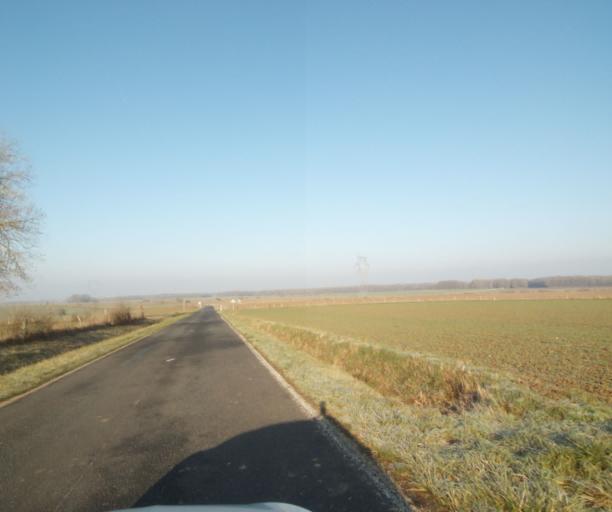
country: FR
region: Champagne-Ardenne
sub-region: Departement de la Haute-Marne
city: Montier-en-Der
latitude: 48.5051
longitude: 4.7343
